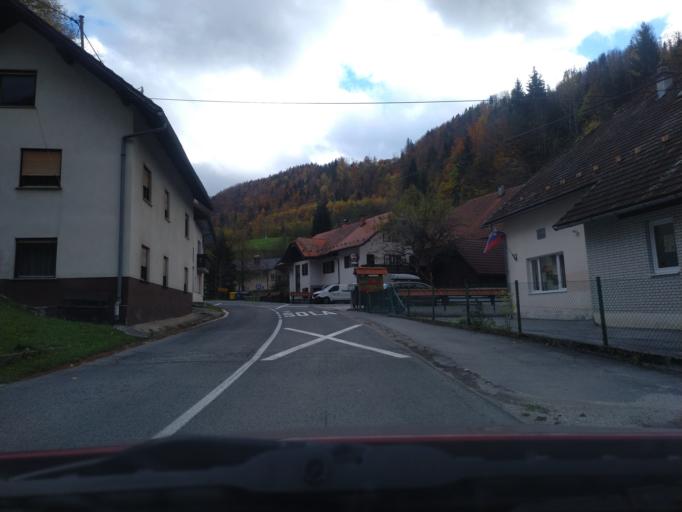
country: SI
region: Kamnik
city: Mekinje
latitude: 46.2633
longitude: 14.6713
